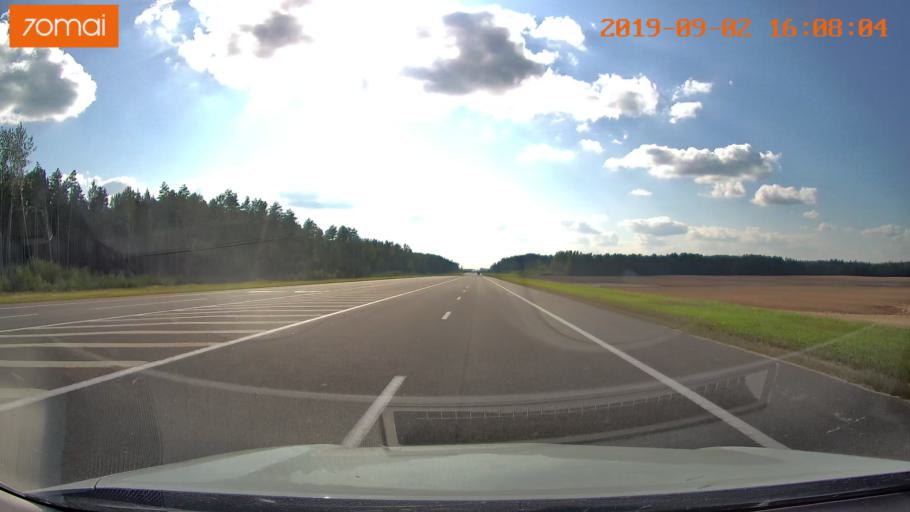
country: BY
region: Minsk
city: Byerazino
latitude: 53.7778
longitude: 28.7391
